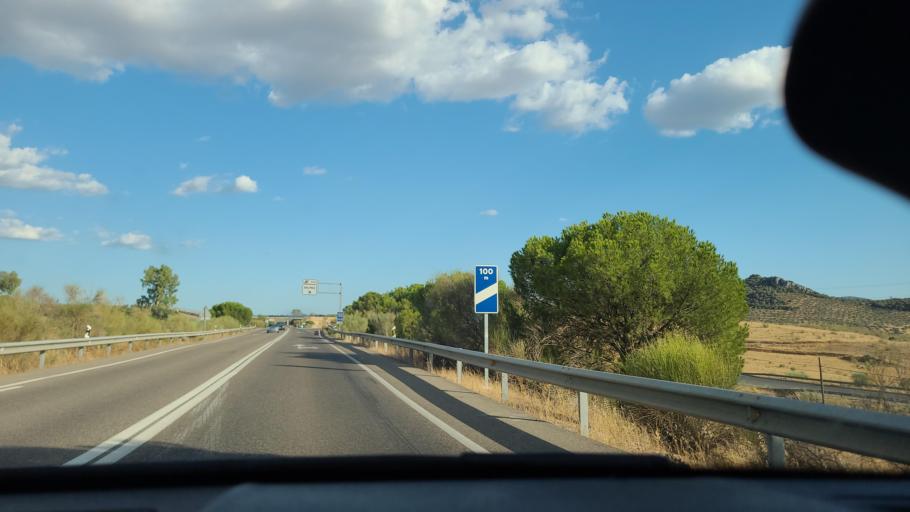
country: ES
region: Andalusia
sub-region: Province of Cordoba
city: Belmez
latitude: 38.2670
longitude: -5.1874
